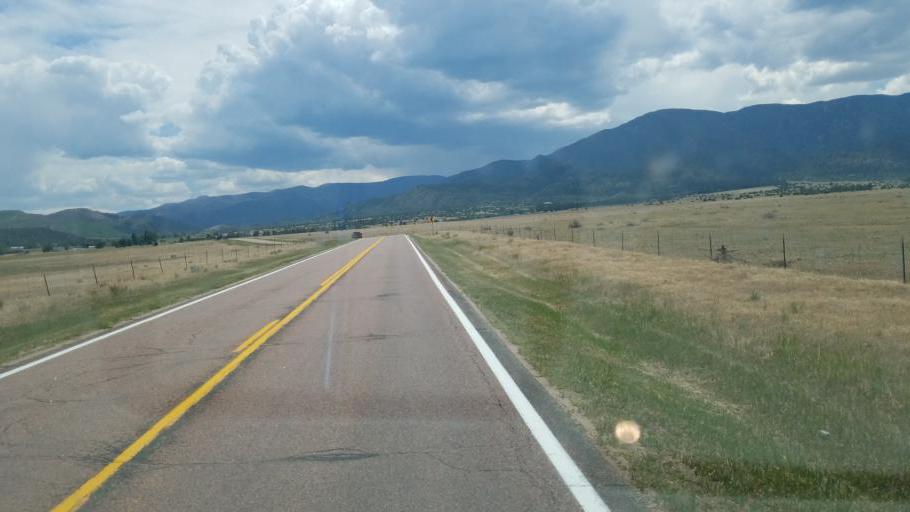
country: US
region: Colorado
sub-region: Fremont County
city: Florence
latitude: 38.2562
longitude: -105.0899
